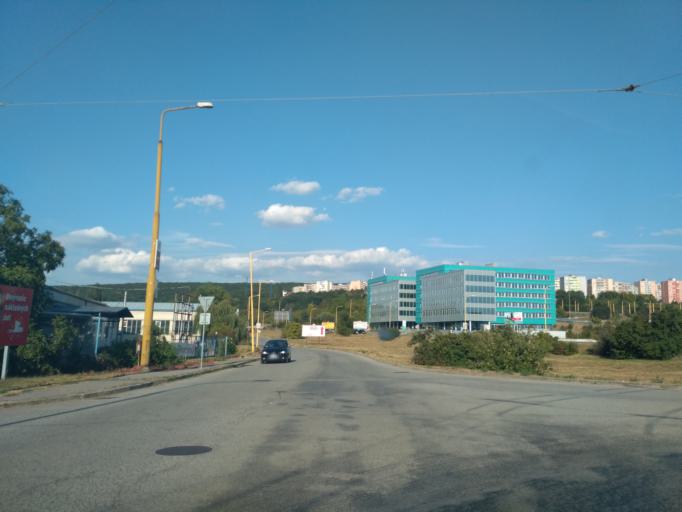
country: SK
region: Kosicky
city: Kosice
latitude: 48.7431
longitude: 21.2656
